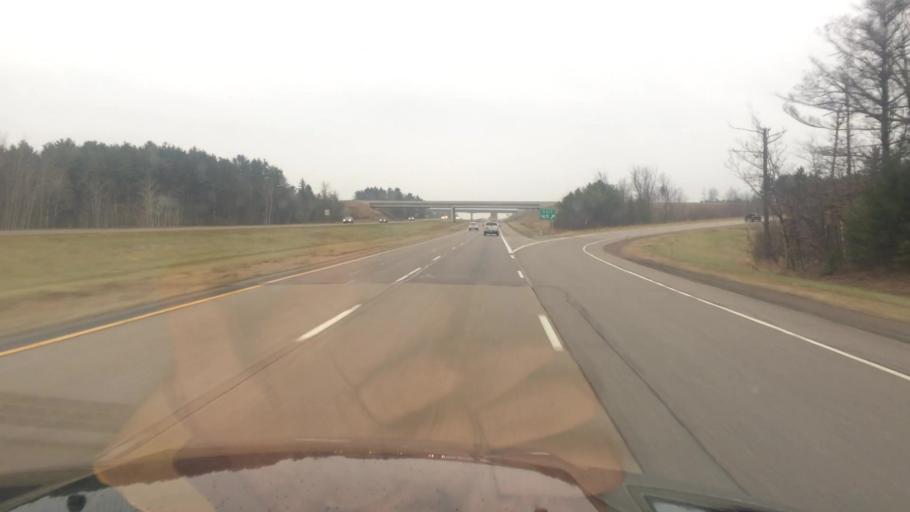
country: US
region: Wisconsin
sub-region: Portage County
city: Stevens Point
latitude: 44.6010
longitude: -89.6175
